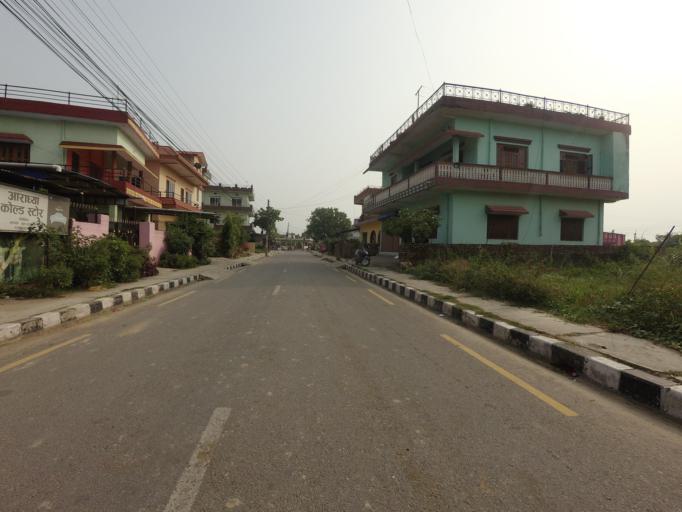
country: NP
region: Western Region
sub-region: Lumbini Zone
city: Bhairahawa
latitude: 27.5262
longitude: 83.4595
